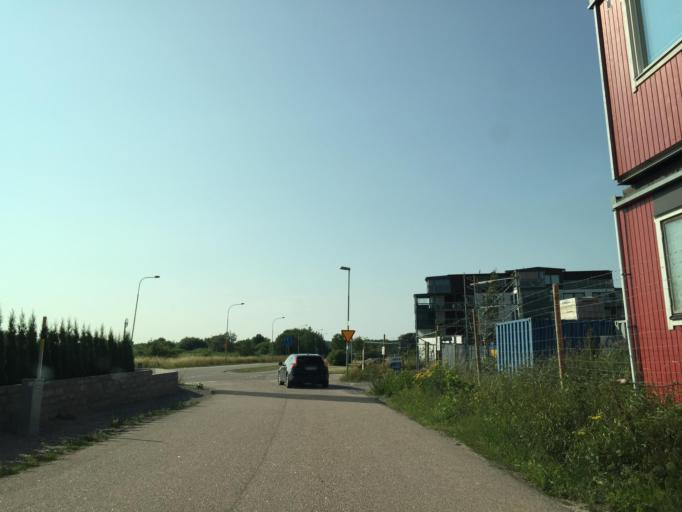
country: SE
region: Vaestra Goetaland
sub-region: Vanersborgs Kommun
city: Vanersborg
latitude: 58.3613
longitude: 12.3184
